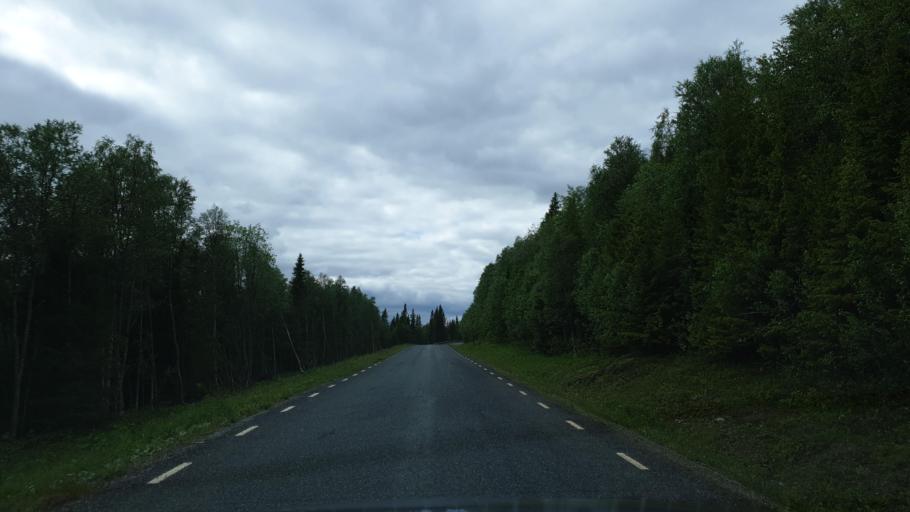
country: NO
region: Nordland
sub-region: Hattfjelldal
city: Hattfjelldal
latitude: 65.4407
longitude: 14.5561
